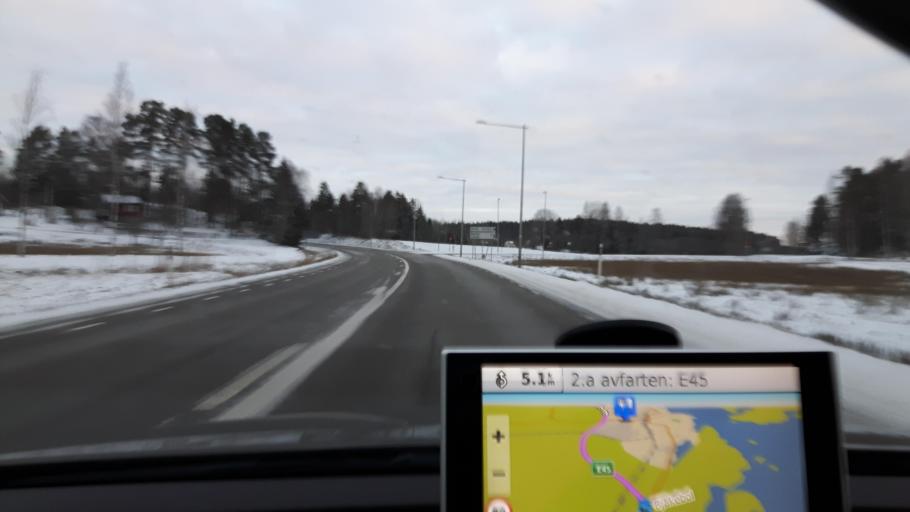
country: SE
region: Vaestra Goetaland
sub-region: Amals Kommun
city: Amal
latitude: 59.0132
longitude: 12.6918
